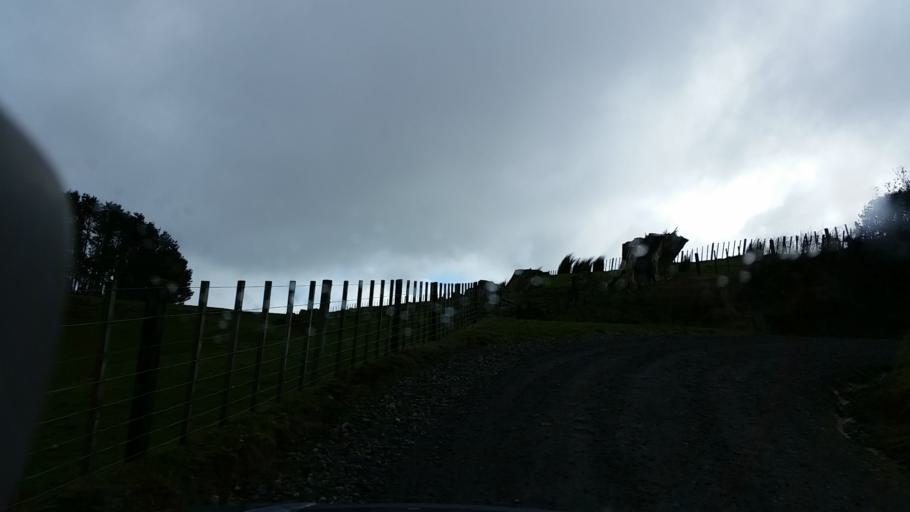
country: NZ
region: Taranaki
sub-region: South Taranaki District
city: Eltham
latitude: -39.2773
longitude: 174.3382
